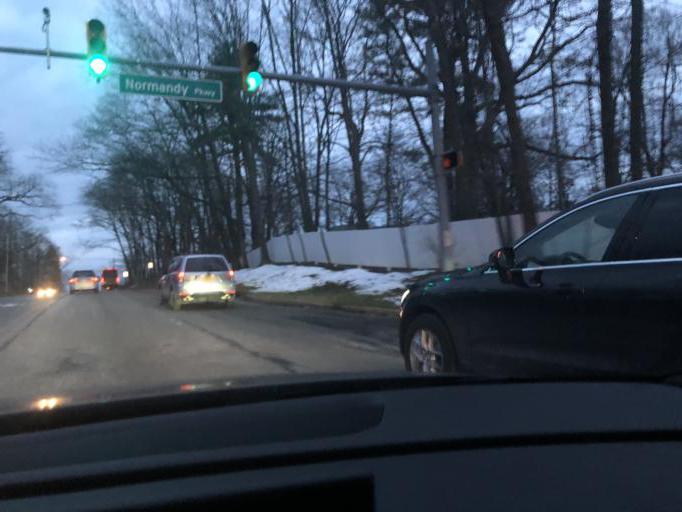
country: US
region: New Jersey
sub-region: Morris County
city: Morristown
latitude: 40.7948
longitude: -74.4480
